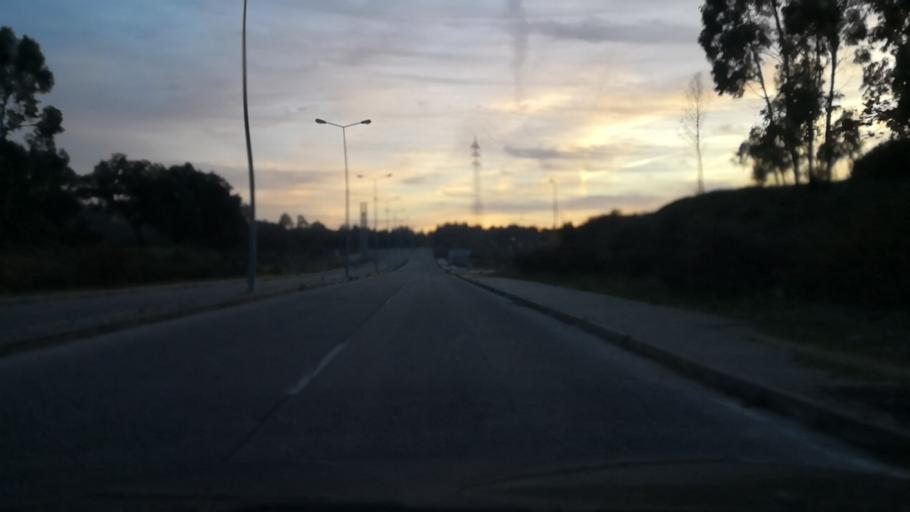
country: PT
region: Setubal
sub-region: Setubal
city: Setubal
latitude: 38.5170
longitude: -8.8511
